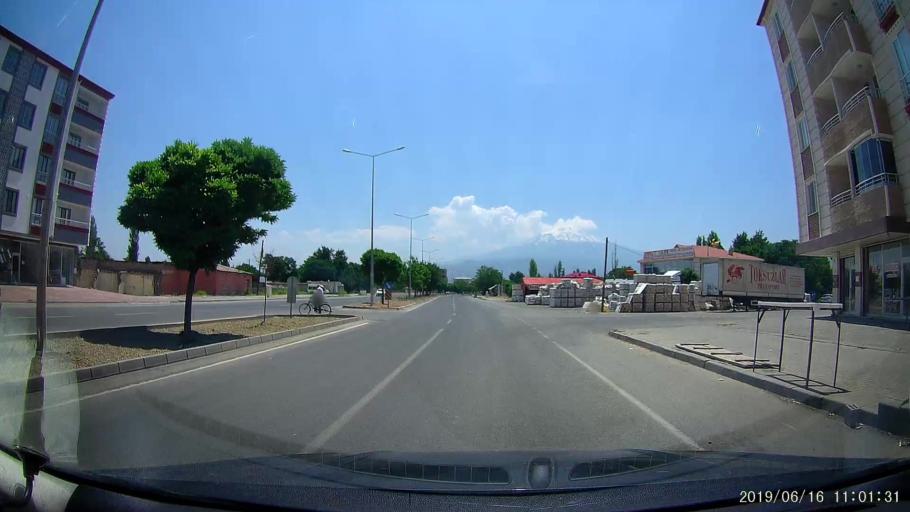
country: TR
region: Igdir
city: Igdir
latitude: 39.9145
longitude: 44.0503
